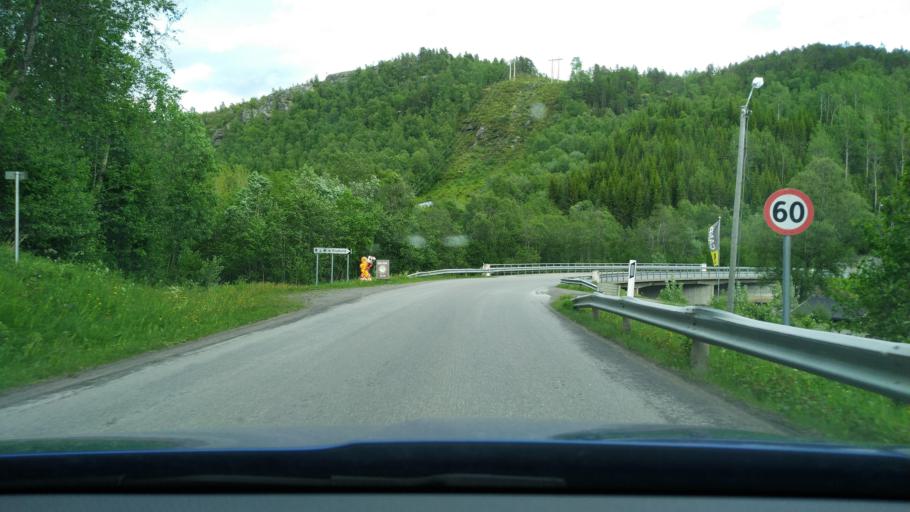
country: NO
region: Troms
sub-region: Salangen
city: Sjovegan
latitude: 68.8659
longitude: 17.8618
